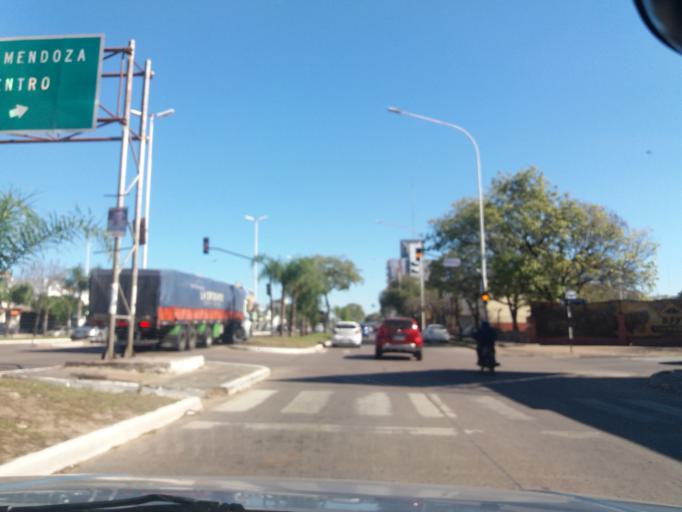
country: AR
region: Corrientes
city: Corrientes
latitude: -27.4761
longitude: -58.8325
